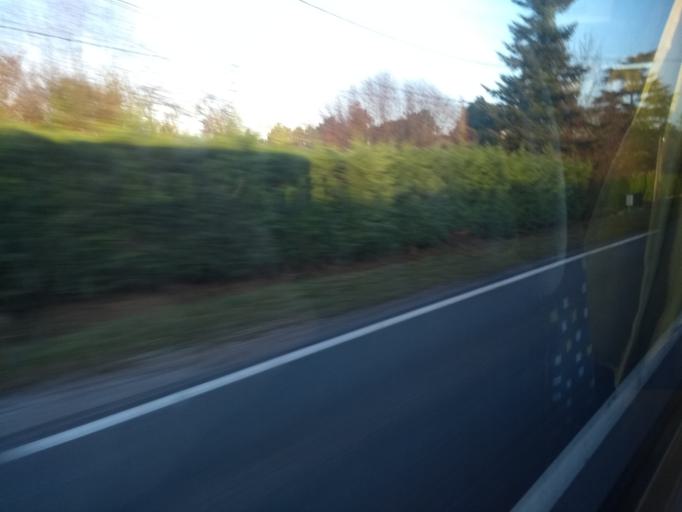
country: FR
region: Aquitaine
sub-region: Departement de la Gironde
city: Le Barp
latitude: 44.6006
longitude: -0.7715
